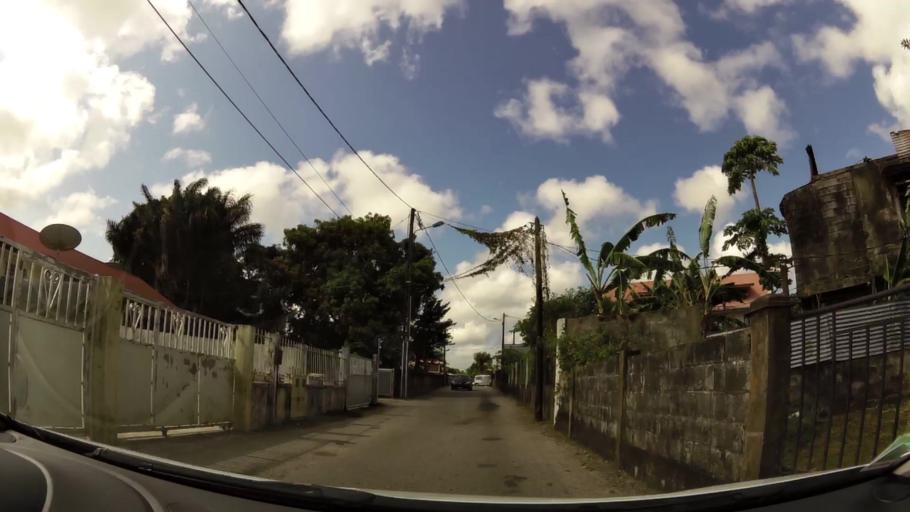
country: GF
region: Guyane
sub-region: Guyane
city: Cayenne
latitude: 4.9303
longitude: -52.3151
